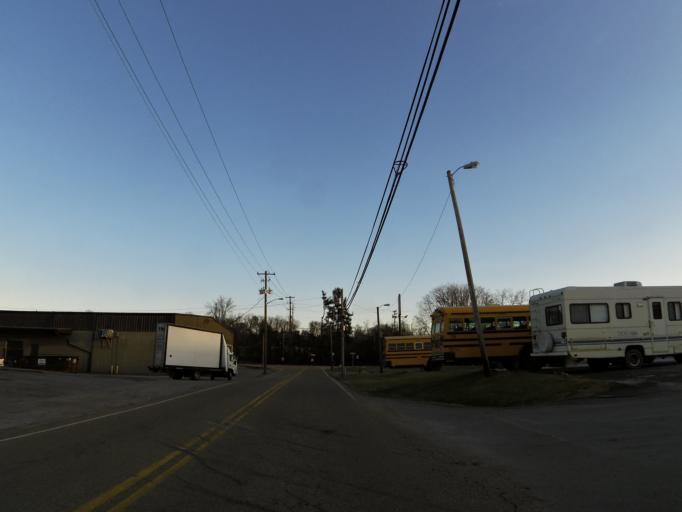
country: US
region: Tennessee
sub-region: Knox County
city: Knoxville
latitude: 36.0099
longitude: -83.8743
